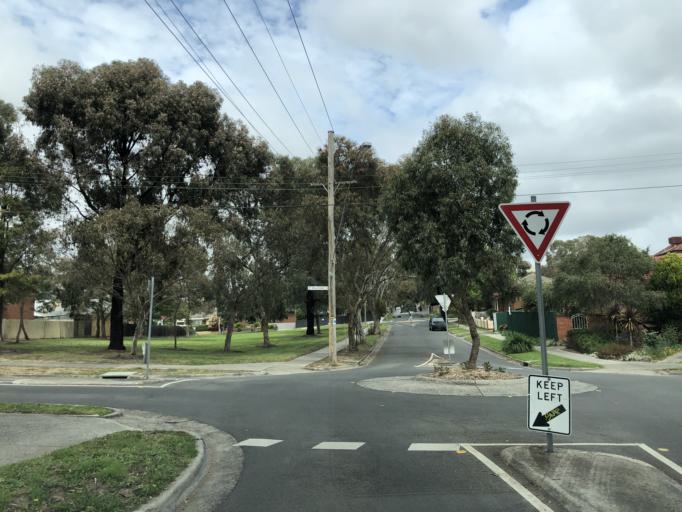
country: AU
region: Victoria
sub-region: Whitehorse
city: Blackburn South
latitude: -37.8393
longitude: 145.1595
